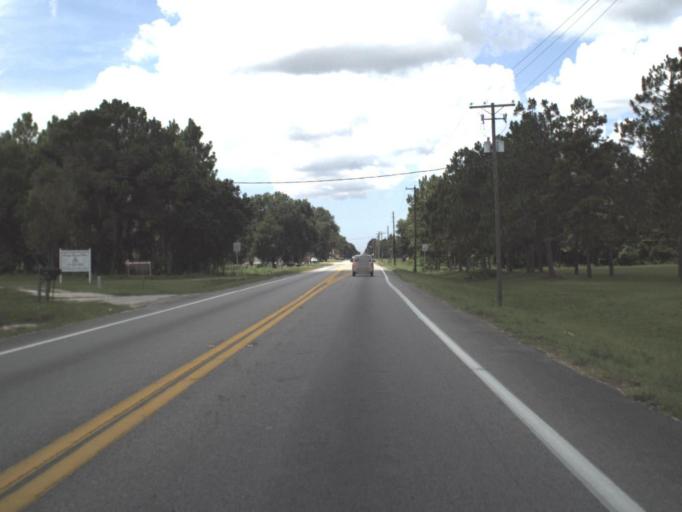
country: US
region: Florida
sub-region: Taylor County
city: Perry
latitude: 30.1104
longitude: -83.5937
